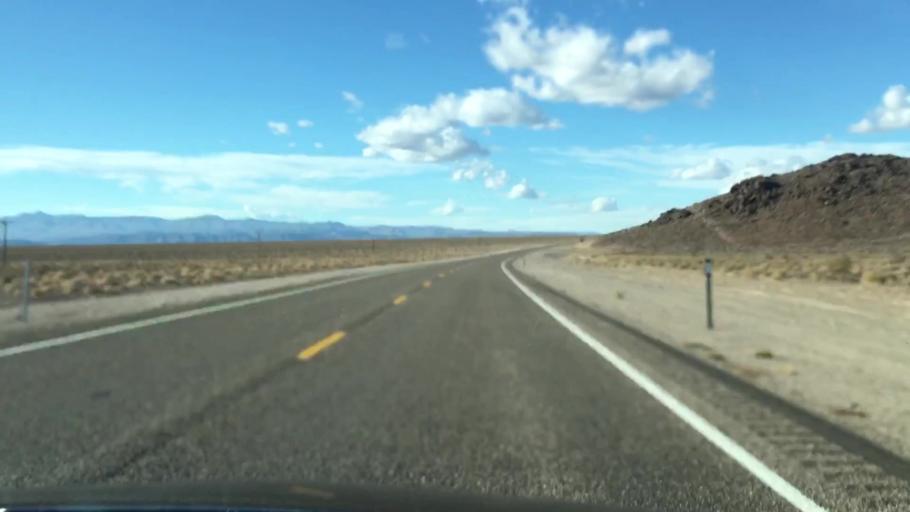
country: US
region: Nevada
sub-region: Nye County
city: Beatty
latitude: 37.1797
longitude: -116.9312
